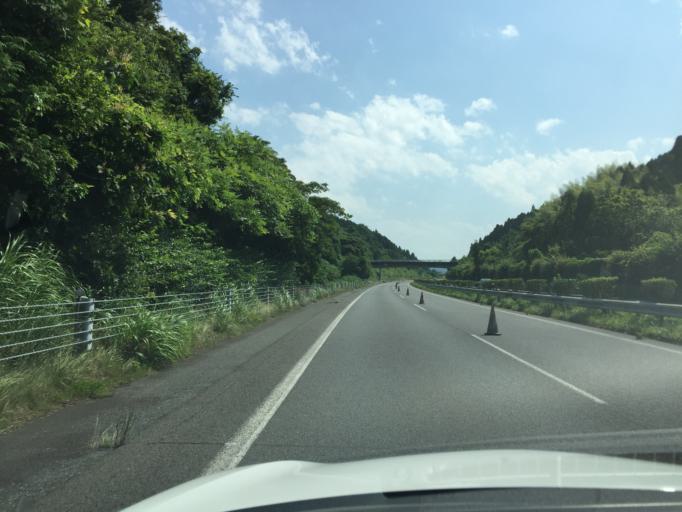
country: JP
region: Ibaraki
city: Kitaibaraki
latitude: 36.9159
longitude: 140.7583
